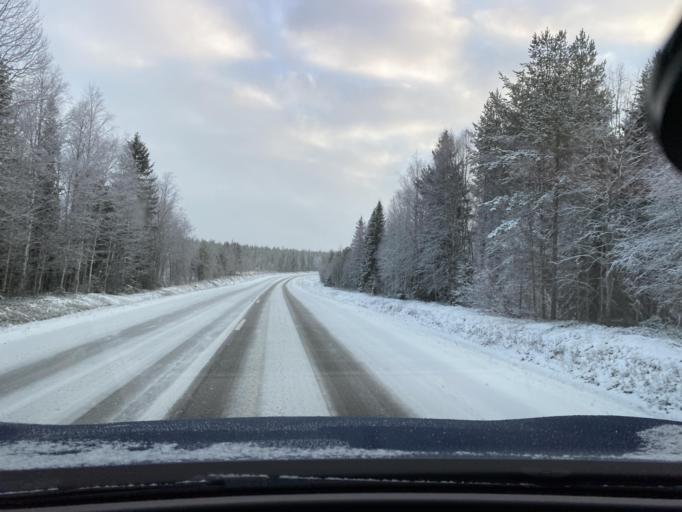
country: FI
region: Lapland
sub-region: Rovaniemi
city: Ranua
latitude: 65.8998
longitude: 26.5295
